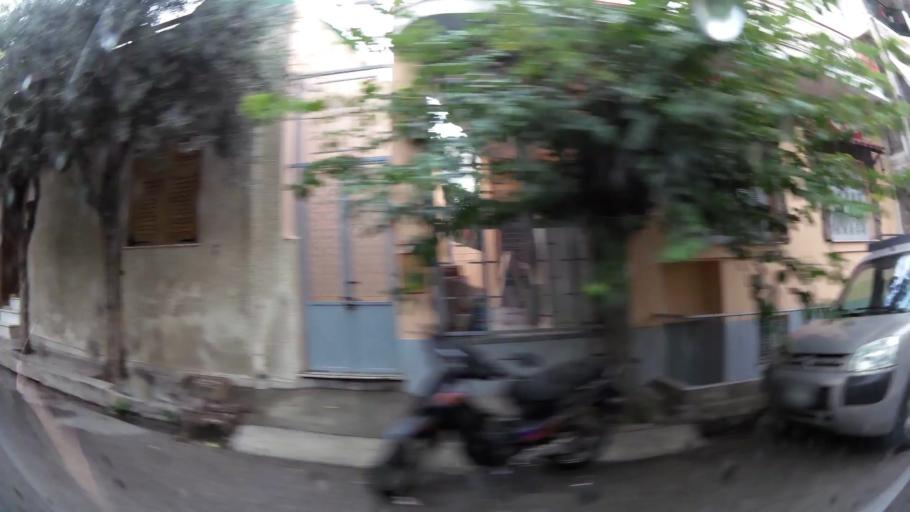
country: GR
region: Attica
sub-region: Nomarchia Athinas
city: Ymittos
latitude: 37.9553
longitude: 23.7507
